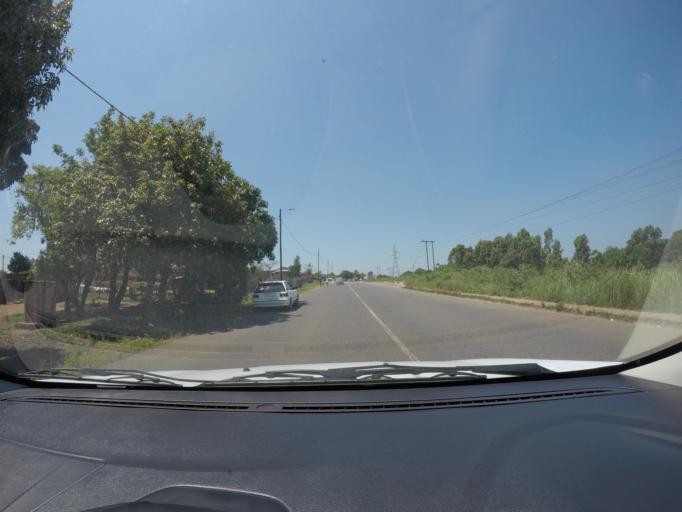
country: ZA
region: KwaZulu-Natal
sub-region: uThungulu District Municipality
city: eSikhawini
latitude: -28.8283
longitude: 31.9431
